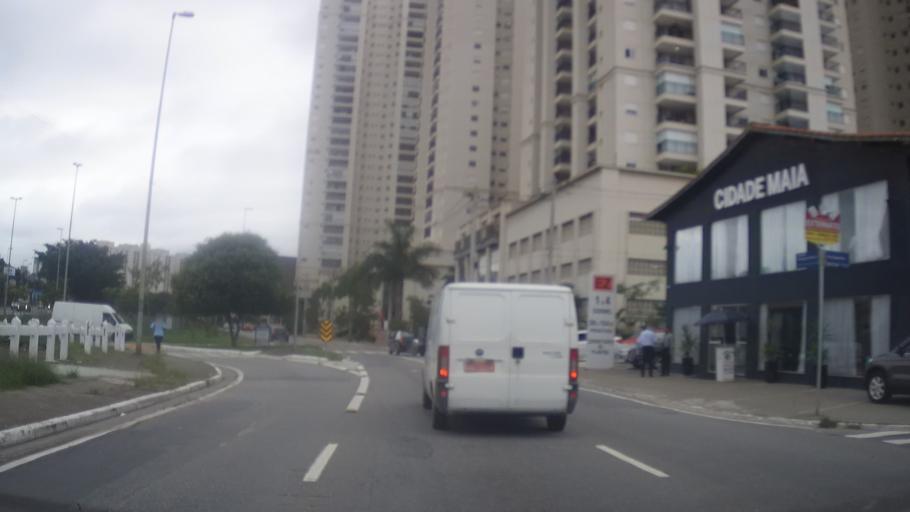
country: BR
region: Sao Paulo
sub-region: Guarulhos
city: Guarulhos
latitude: -23.4404
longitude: -46.5440
